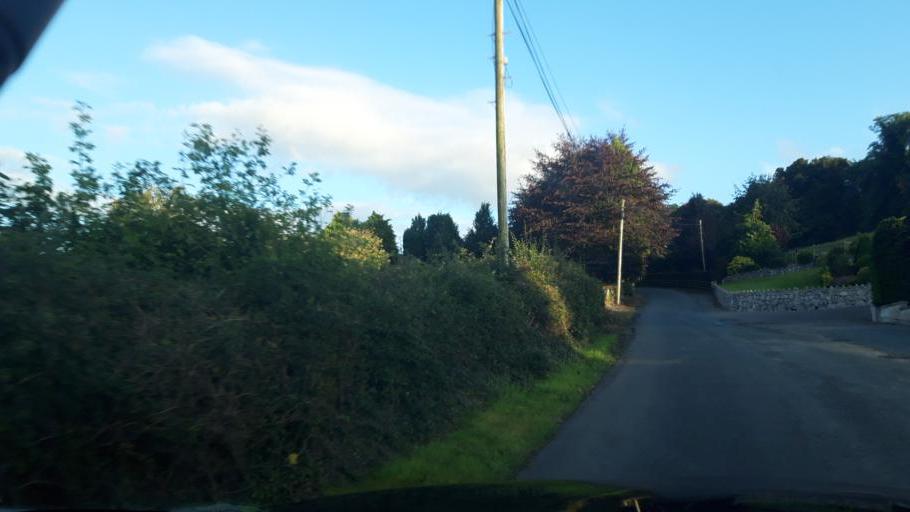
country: IE
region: Leinster
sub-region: An Iarmhi
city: Athlone
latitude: 53.4348
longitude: -7.8576
